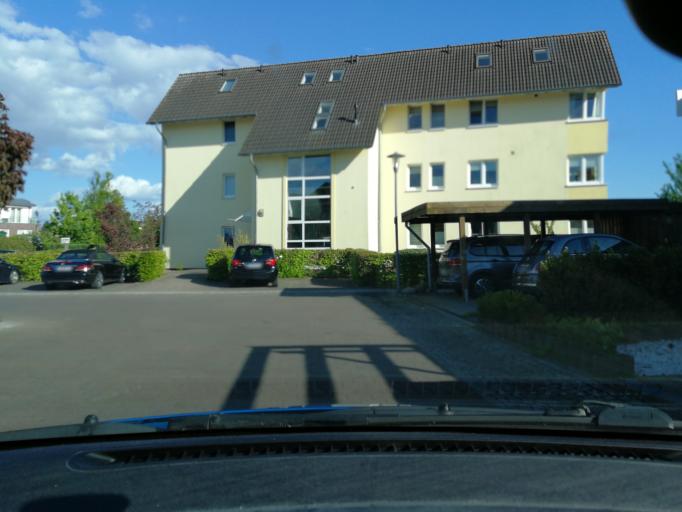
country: DE
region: Lower Saxony
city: Winsen
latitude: 53.3639
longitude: 10.1937
